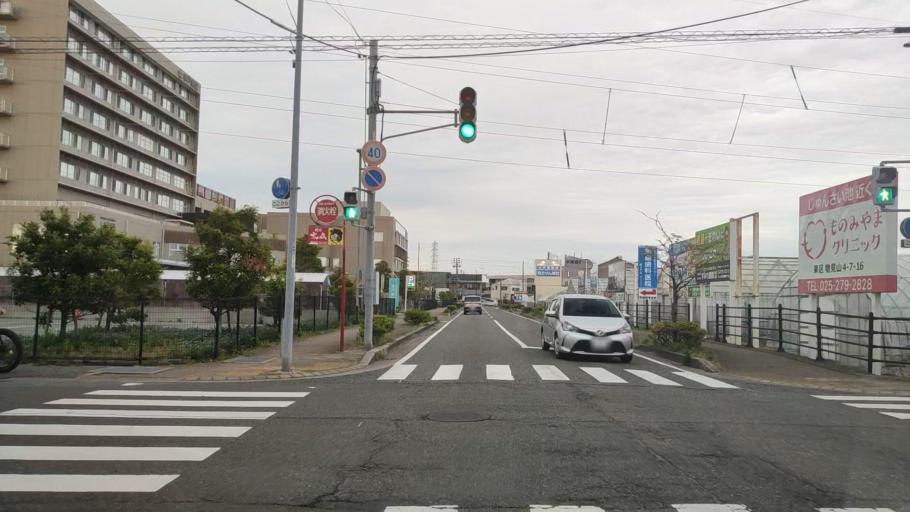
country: JP
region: Niigata
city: Kameda-honcho
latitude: 37.9144
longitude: 139.0986
